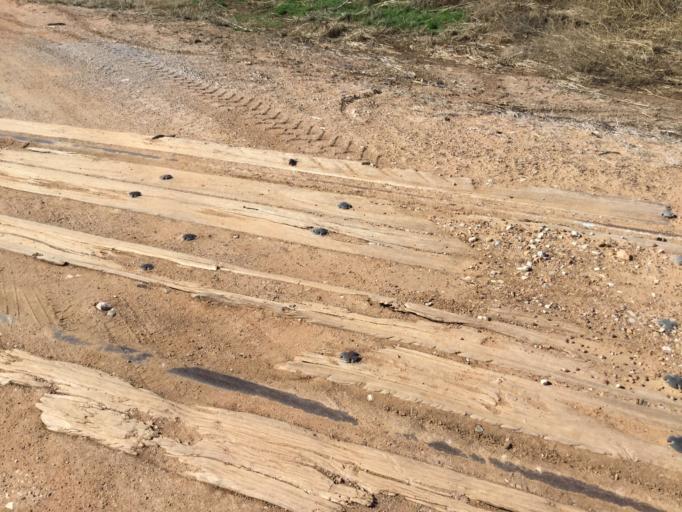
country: US
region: Kansas
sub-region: Barber County
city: Kiowa
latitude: 37.0020
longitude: -98.4854
